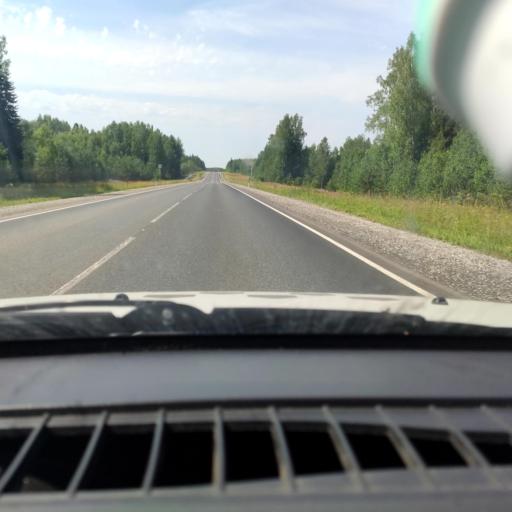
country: RU
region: Perm
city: Siva
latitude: 58.3926
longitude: 54.5334
